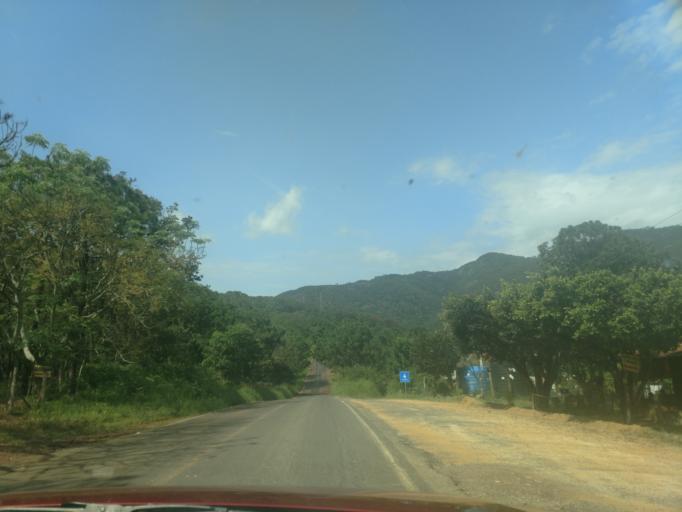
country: MX
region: Jalisco
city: Talpa de Allende
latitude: 20.4342
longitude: -104.7856
